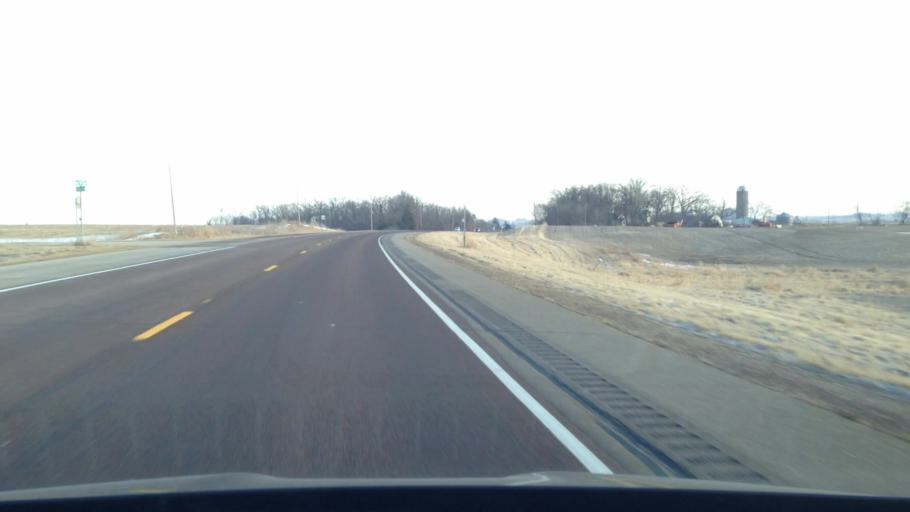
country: US
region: Minnesota
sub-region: Goodhue County
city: Zumbrota
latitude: 44.3390
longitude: -92.6353
